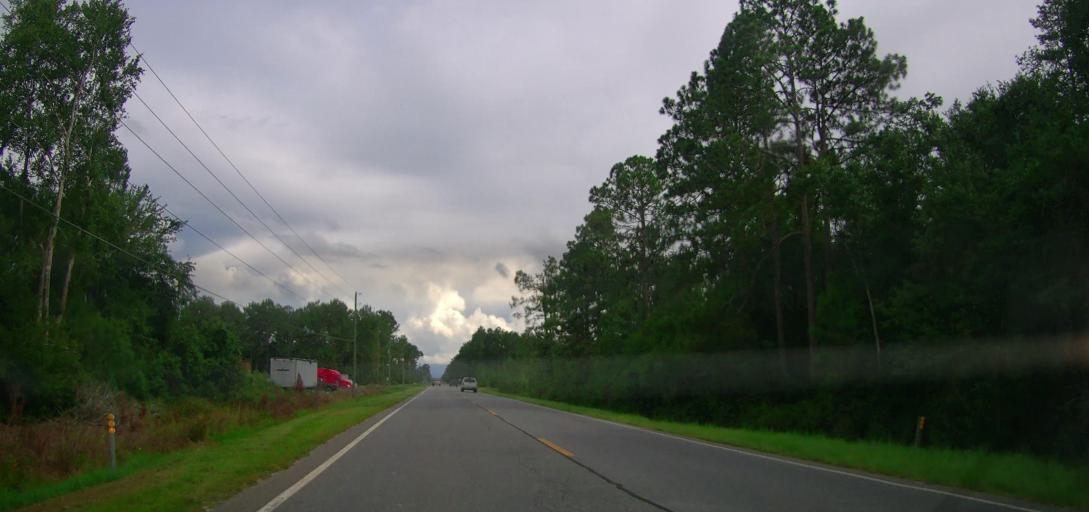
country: US
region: Georgia
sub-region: Wayne County
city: Jesup
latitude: 31.6411
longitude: -81.9057
